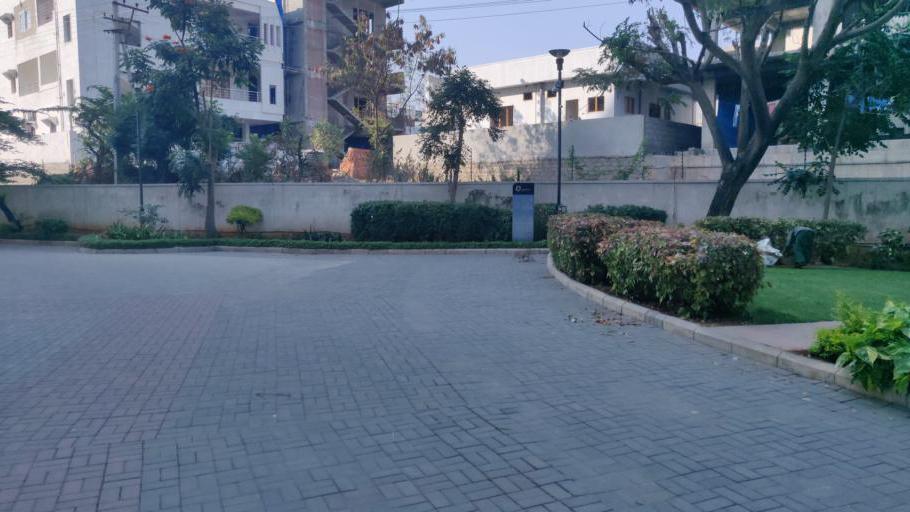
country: IN
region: Telangana
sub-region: Medak
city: Serilingampalle
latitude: 17.4277
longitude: 78.3318
